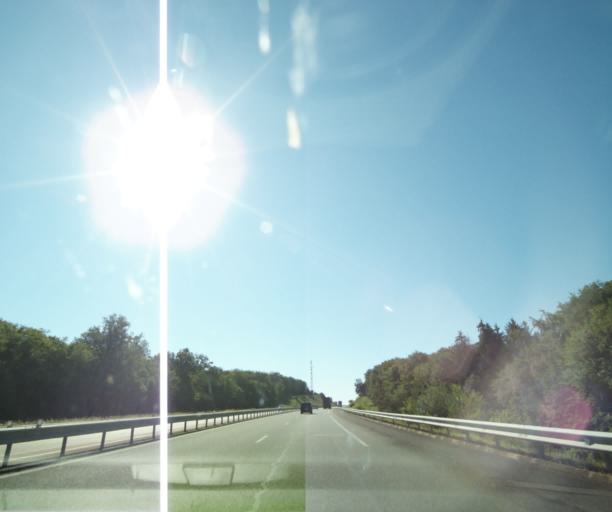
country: FR
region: Champagne-Ardenne
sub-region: Departement de l'Aube
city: Ville-sous-la-Ferte
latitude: 48.0870
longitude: 4.8529
